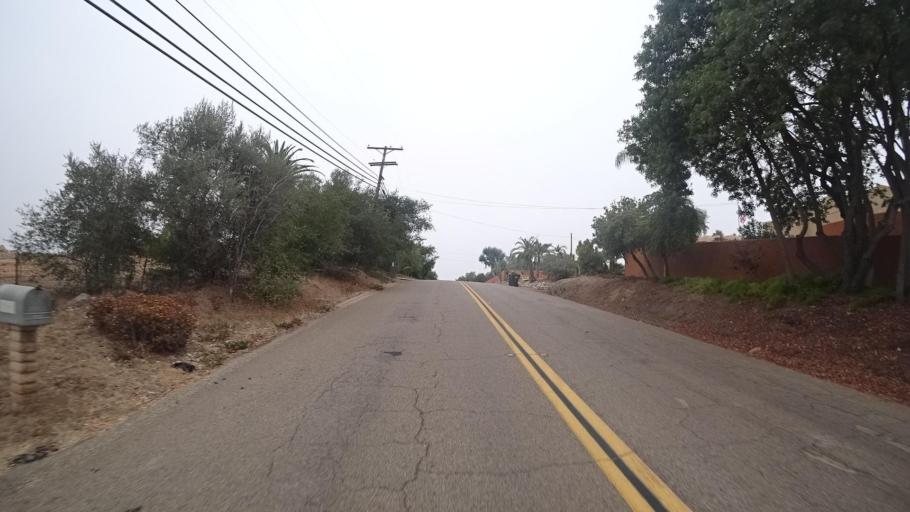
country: US
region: California
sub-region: San Diego County
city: Fallbrook
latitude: 33.3875
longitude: -117.2152
